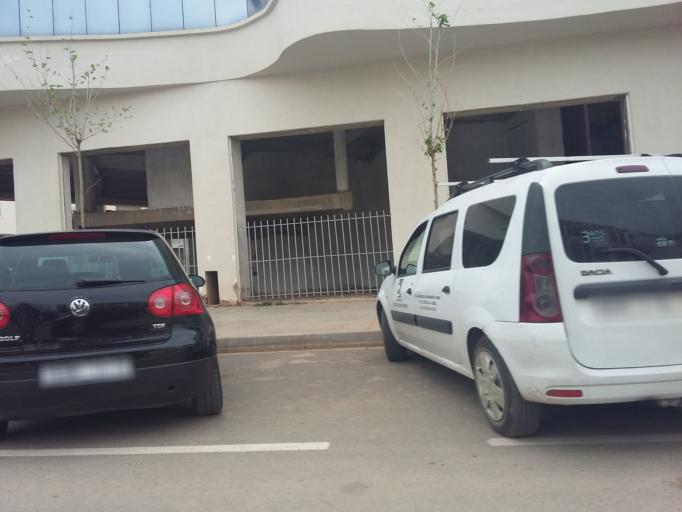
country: MA
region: Fes-Boulemane
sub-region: Fes
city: Fes
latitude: 34.0013
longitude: -5.0112
